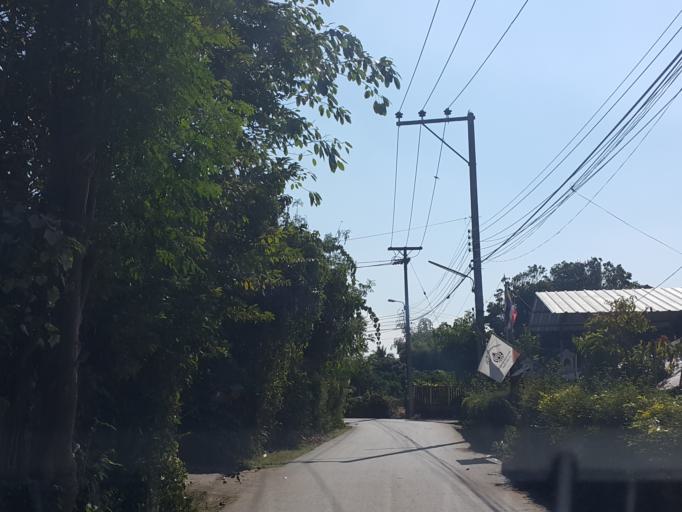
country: TH
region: Chiang Mai
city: San Sai
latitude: 18.8840
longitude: 98.9933
